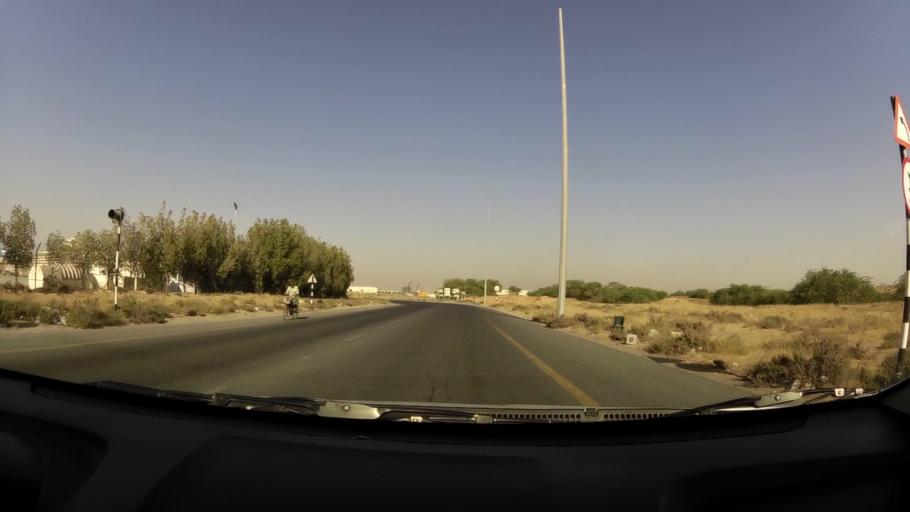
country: AE
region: Umm al Qaywayn
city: Umm al Qaywayn
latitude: 25.4425
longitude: 55.5573
